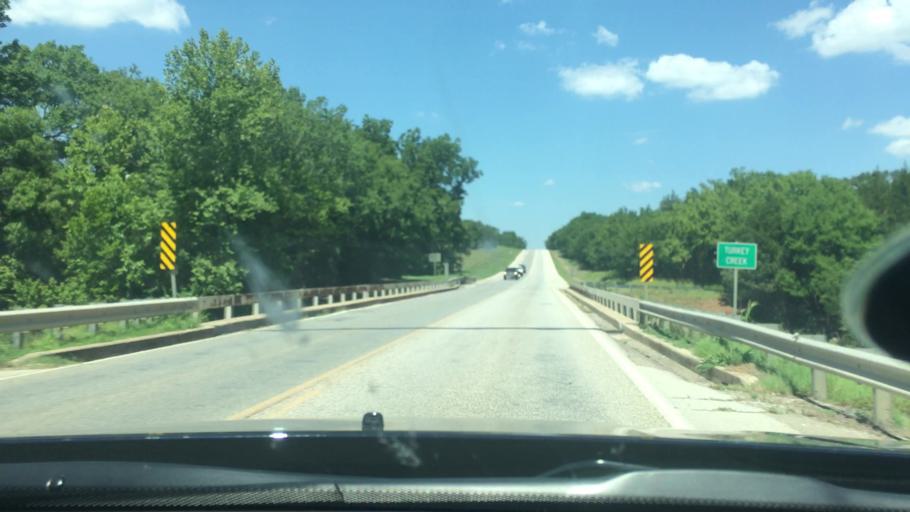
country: US
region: Oklahoma
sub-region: Marshall County
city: Oakland
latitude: 34.1755
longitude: -96.8579
